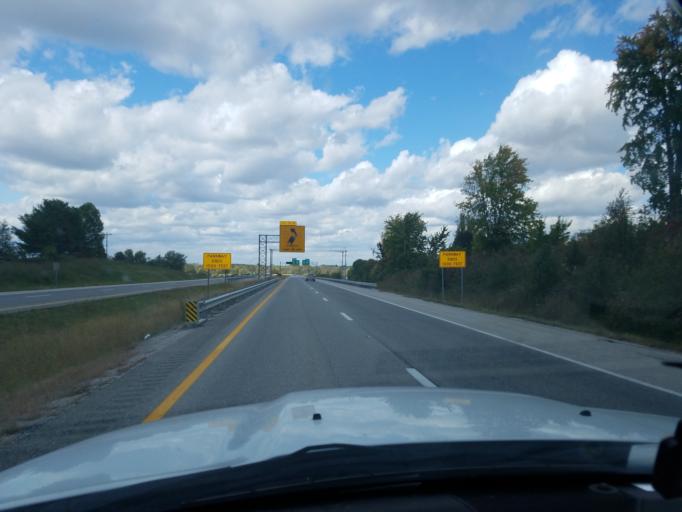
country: US
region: Kentucky
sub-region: Daviess County
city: Owensboro
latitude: 37.7359
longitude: -87.0680
